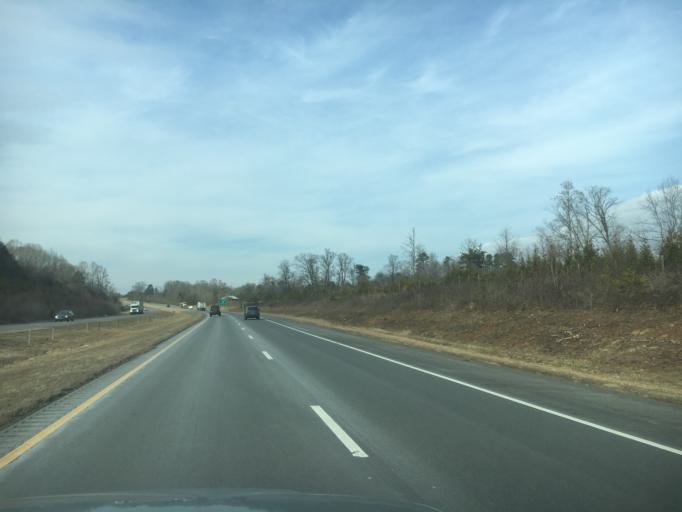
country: US
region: North Carolina
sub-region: Catawba County
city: Newton
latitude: 35.6245
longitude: -81.2899
